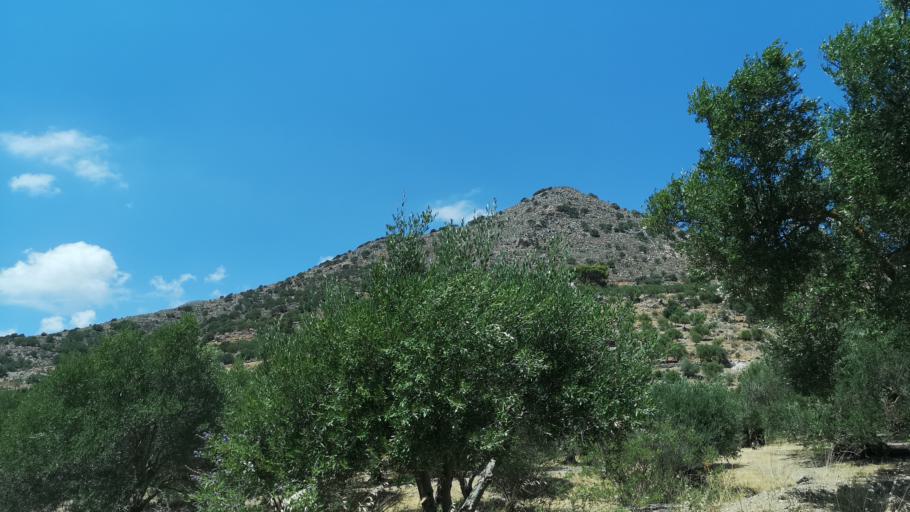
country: GR
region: Crete
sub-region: Nomos Lasithiou
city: Neapoli
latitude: 35.2478
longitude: 25.6279
